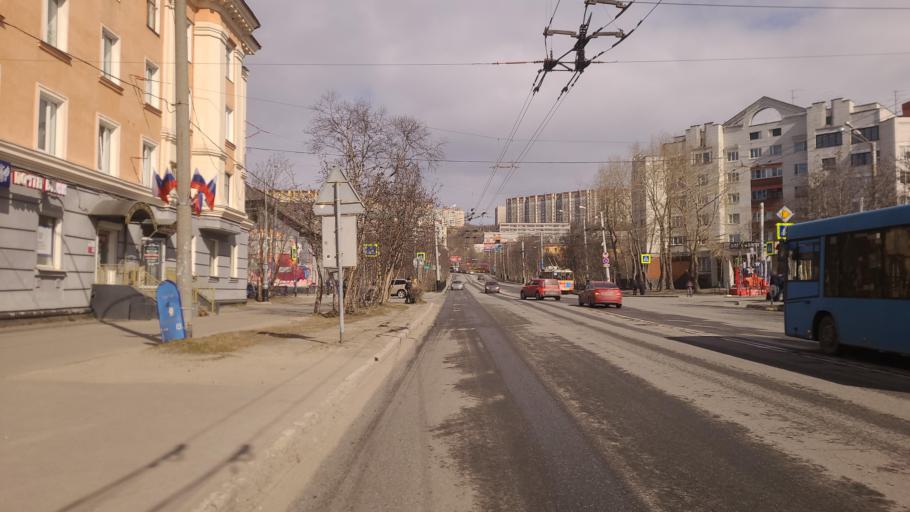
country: RU
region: Murmansk
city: Murmansk
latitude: 68.9782
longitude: 33.0878
